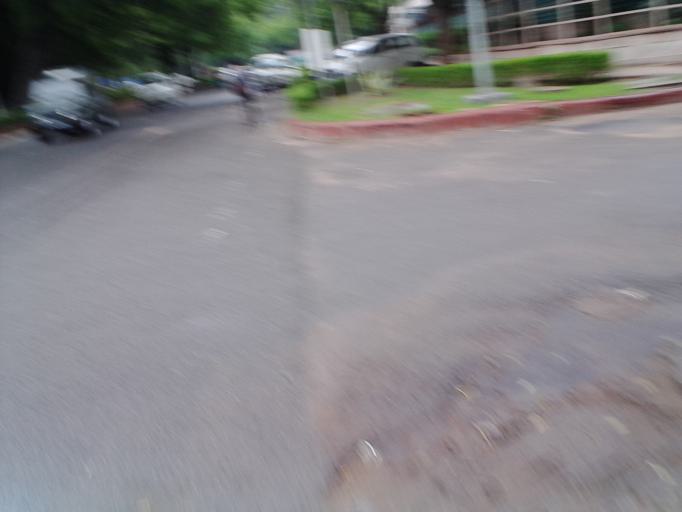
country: IN
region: NCT
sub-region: New Delhi
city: New Delhi
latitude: 28.6101
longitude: 77.2356
